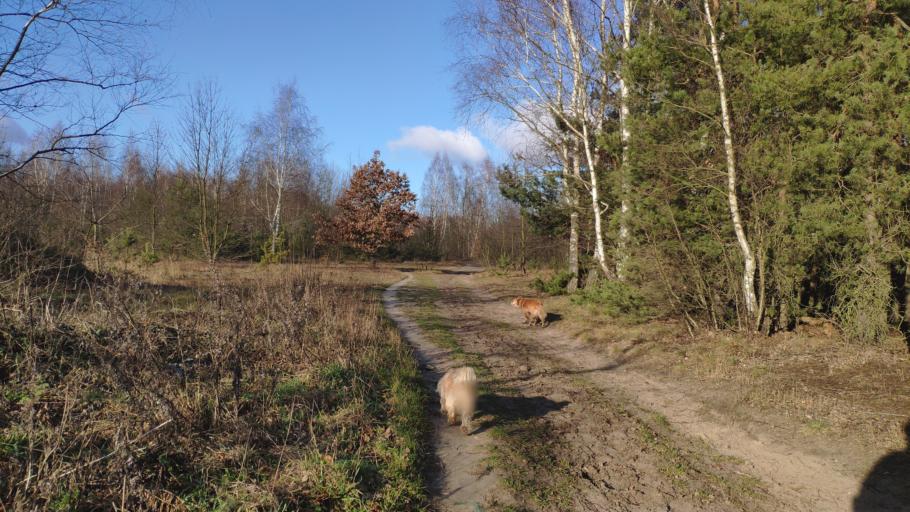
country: PL
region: Lodz Voivodeship
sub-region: Powiat pabianicki
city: Ksawerow
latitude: 51.7283
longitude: 19.4111
